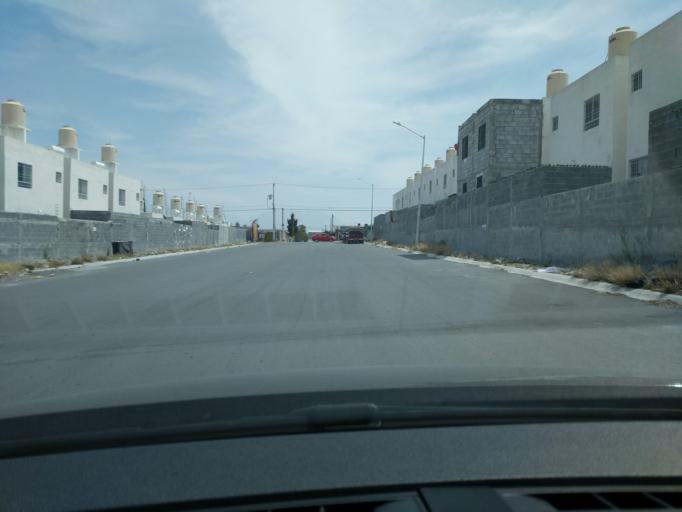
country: MX
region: Coahuila
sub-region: Arteaga
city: Arteaga
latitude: 25.4240
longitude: -100.9115
